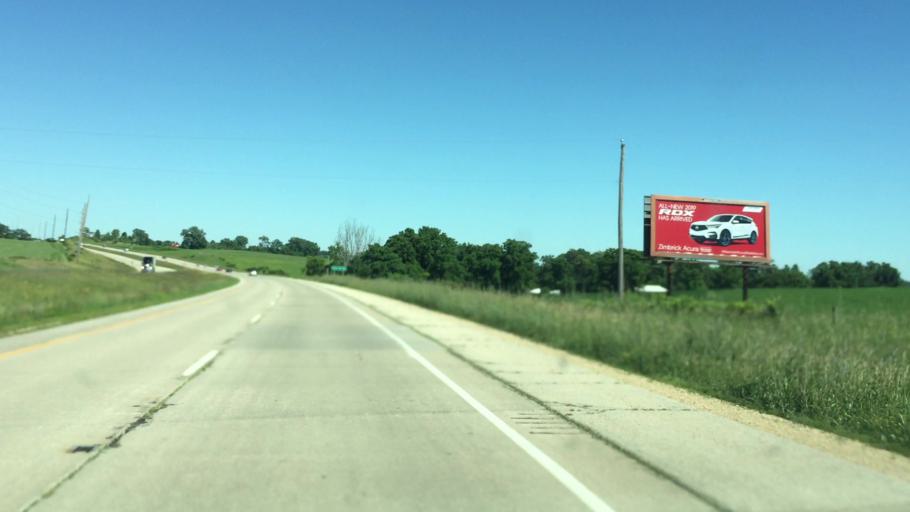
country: US
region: Wisconsin
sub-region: Dane County
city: Mount Horeb
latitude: 42.9885
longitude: -89.6508
